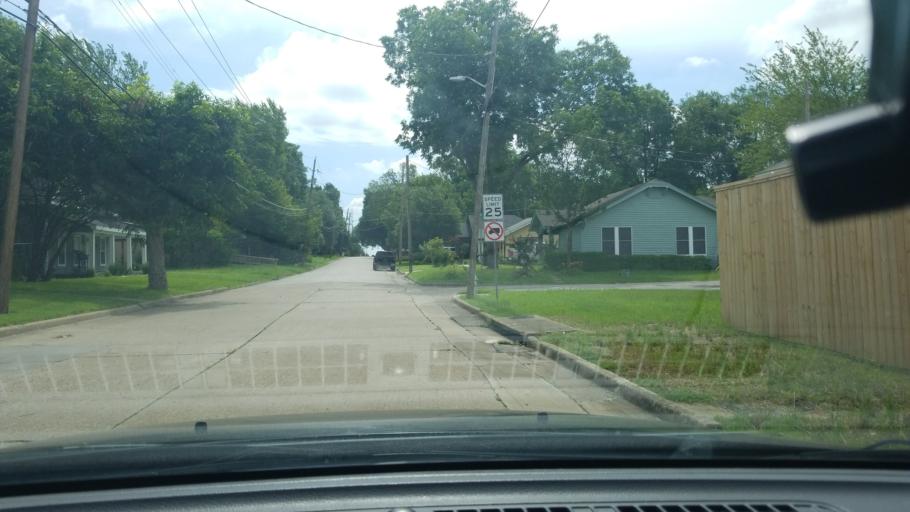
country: US
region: Texas
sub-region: Dallas County
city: Mesquite
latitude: 32.7685
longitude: -96.5969
